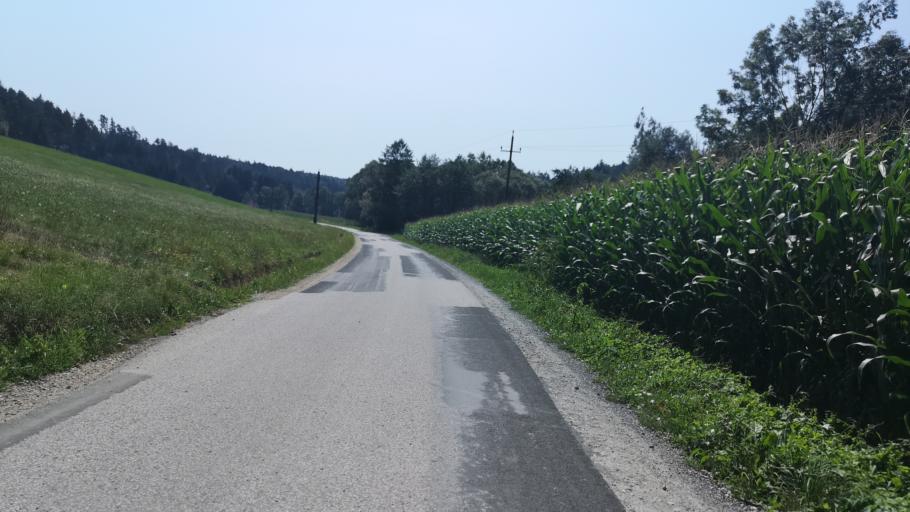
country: AT
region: Styria
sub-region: Politischer Bezirk Deutschlandsberg
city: Sankt Josef (Weststeiermark)
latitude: 46.8908
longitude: 15.3668
